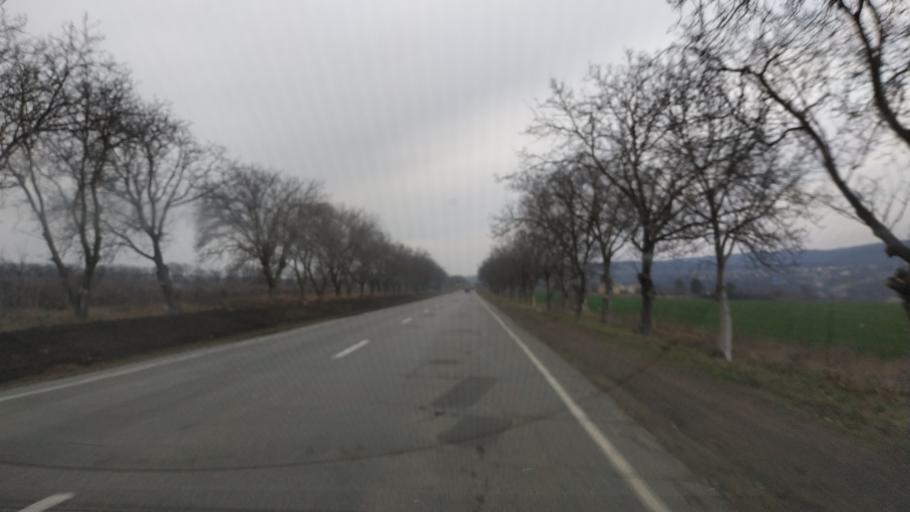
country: MD
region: Hincesti
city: Hincesti
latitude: 46.7883
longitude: 28.5237
